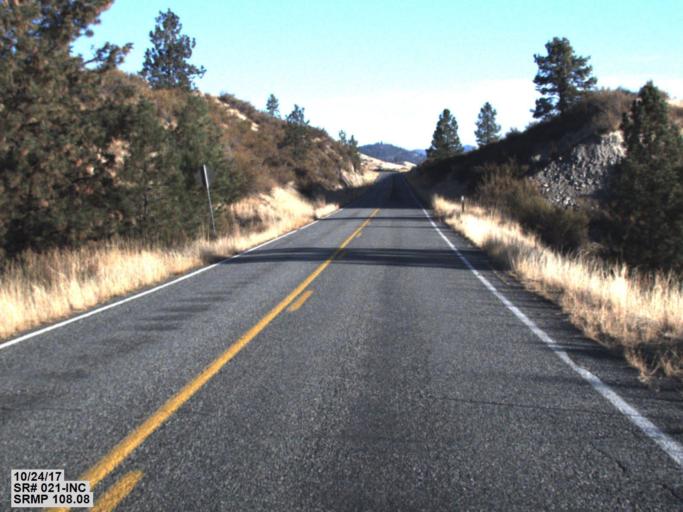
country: US
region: Washington
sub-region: Okanogan County
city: Coulee Dam
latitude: 47.9650
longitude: -118.7001
